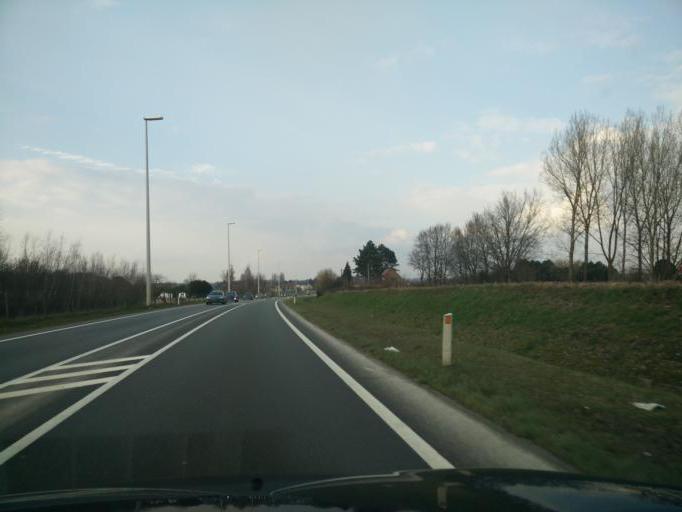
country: BE
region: Flanders
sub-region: Provincie Oost-Vlaanderen
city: Oosterzele
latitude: 50.9134
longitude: 3.8181
